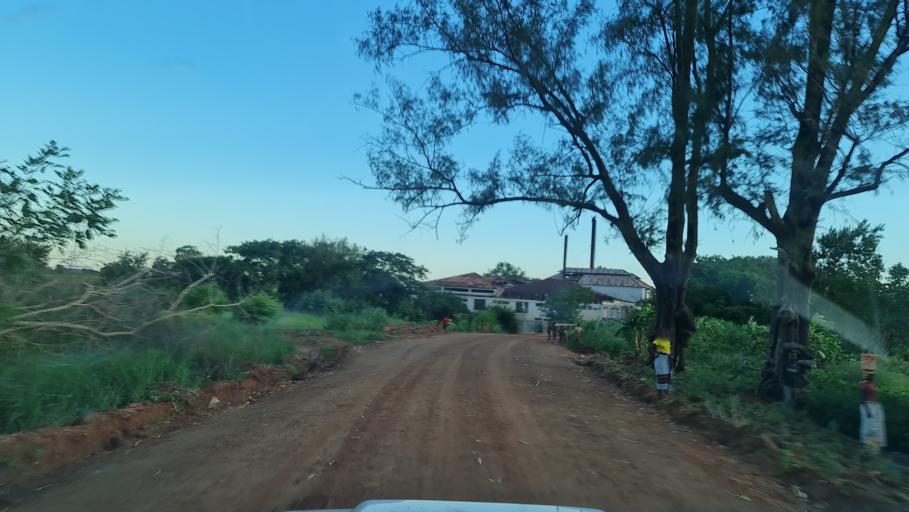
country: MZ
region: Nampula
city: Ilha de Mocambique
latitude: -14.9846
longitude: 40.0949
